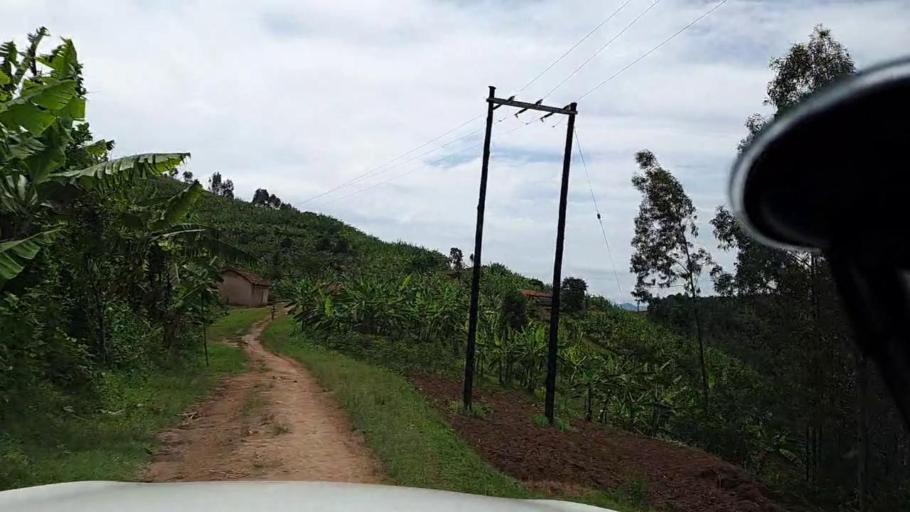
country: RW
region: Southern Province
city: Gitarama
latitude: -2.0789
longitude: 29.6667
